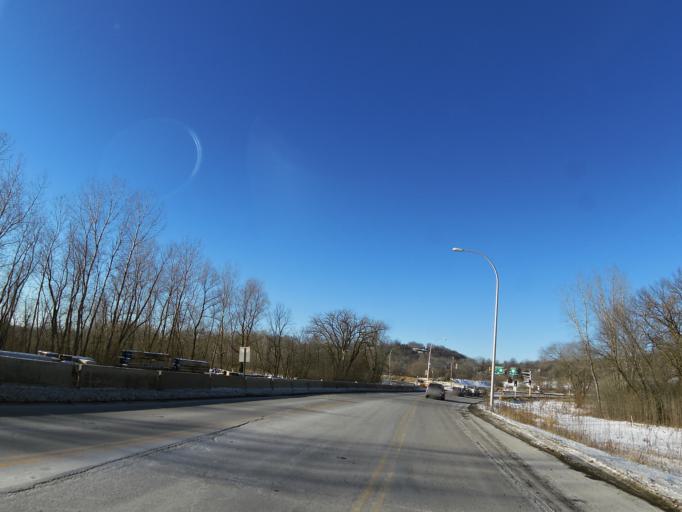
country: US
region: Minnesota
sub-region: Scott County
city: Shakopee
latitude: 44.8095
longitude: -93.5367
